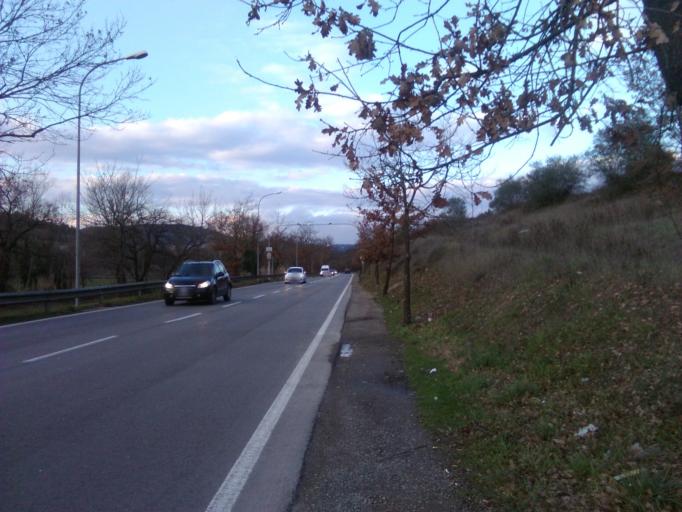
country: IT
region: Umbria
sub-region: Provincia di Perugia
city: Lacugnano
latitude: 43.0886
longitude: 12.3594
